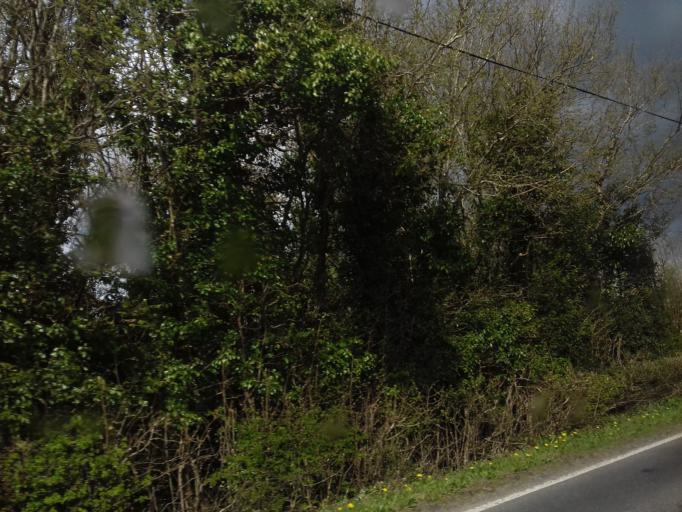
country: IE
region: Ulster
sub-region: County Donegal
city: Ballyshannon
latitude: 54.4702
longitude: -7.9927
